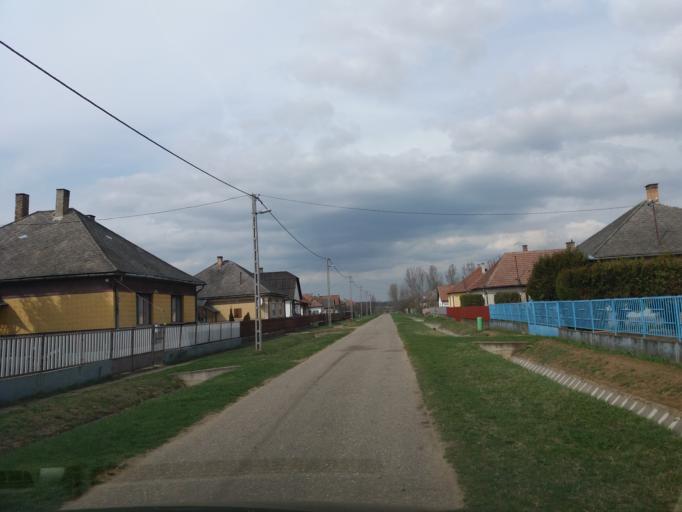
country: HU
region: Szabolcs-Szatmar-Bereg
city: Petnehaza
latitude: 48.0527
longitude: 22.0373
